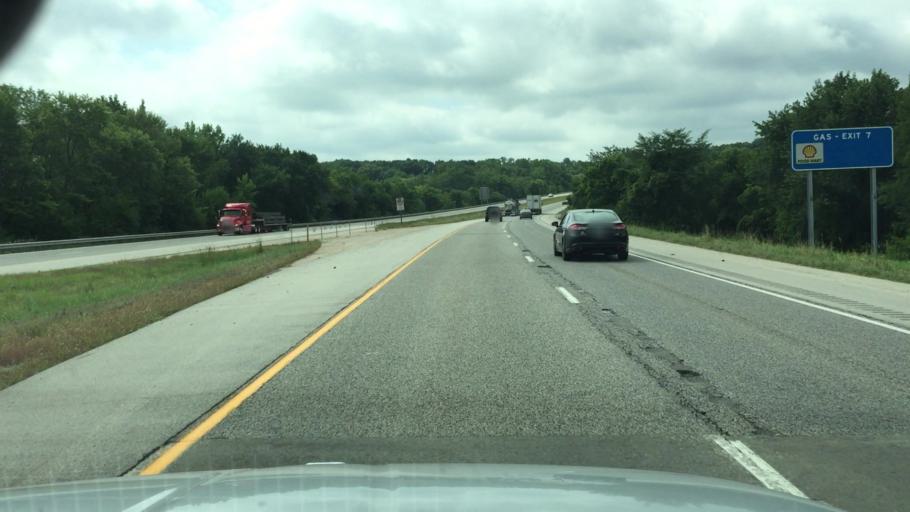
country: US
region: Illinois
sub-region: Henry County
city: Colona
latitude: 41.5071
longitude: -90.3395
